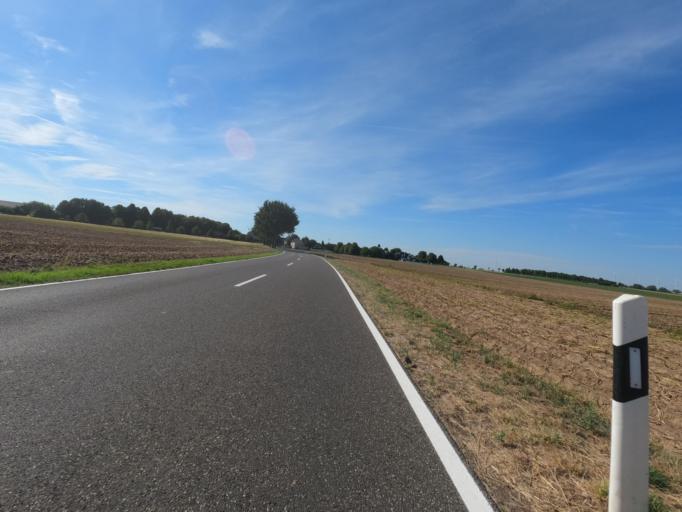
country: DE
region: North Rhine-Westphalia
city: Erkelenz
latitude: 51.0387
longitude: 6.3496
